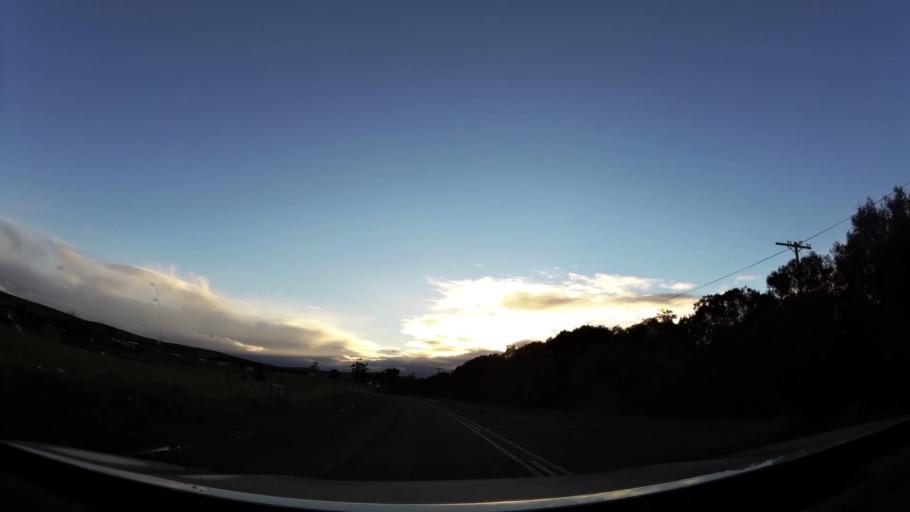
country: ZA
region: Western Cape
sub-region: Eden District Municipality
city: Riversdale
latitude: -34.0792
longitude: 20.9274
